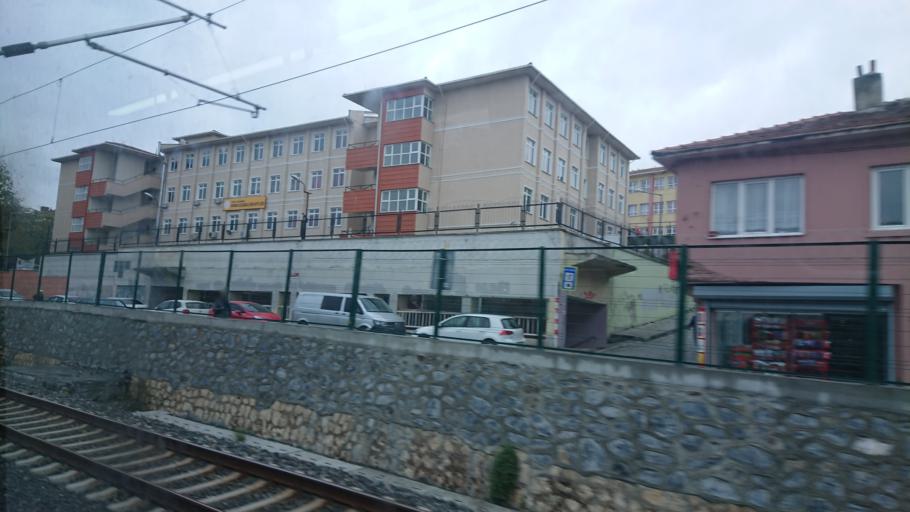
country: TR
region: Istanbul
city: Mahmutbey
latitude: 40.9907
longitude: 28.7724
